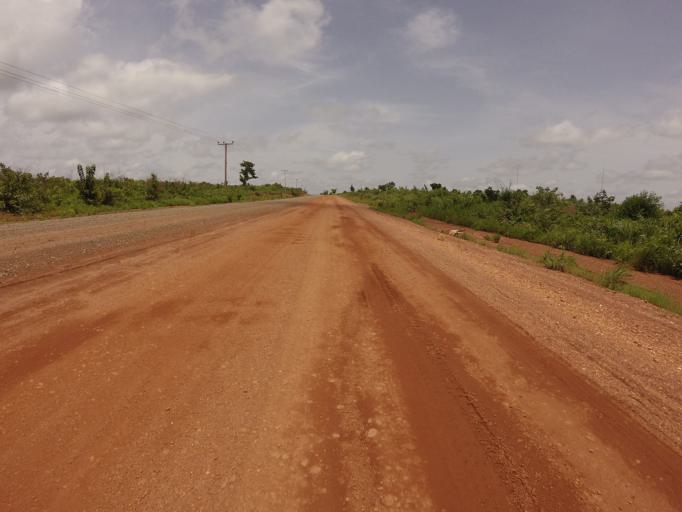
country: GH
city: Kpandae
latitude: 8.6238
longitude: 0.2264
